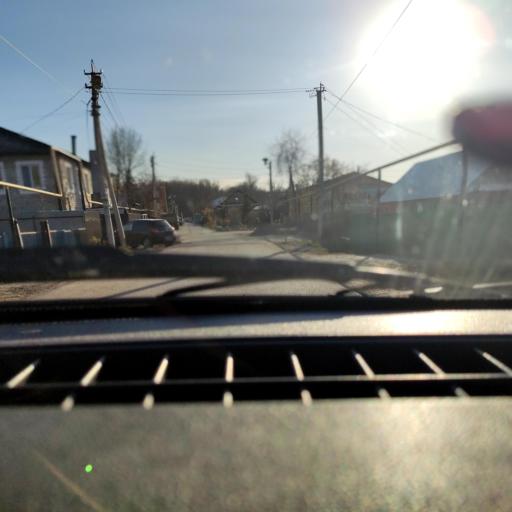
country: RU
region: Bashkortostan
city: Ufa
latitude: 54.6863
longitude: 55.9582
